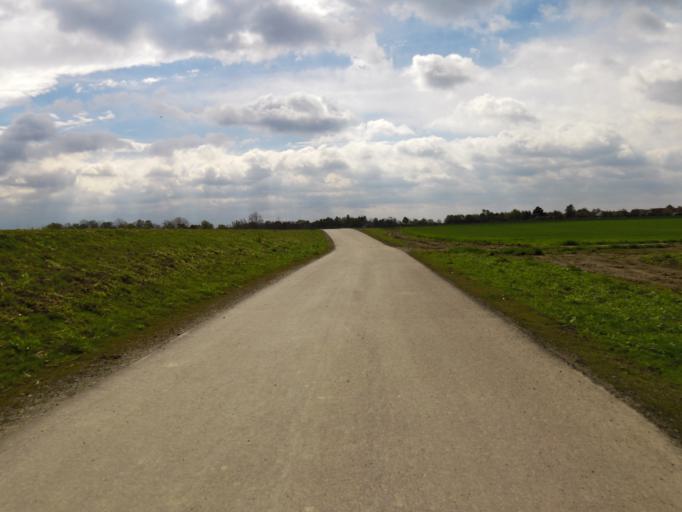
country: DE
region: Rheinland-Pfalz
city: Eich
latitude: 49.6888
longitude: 8.3954
